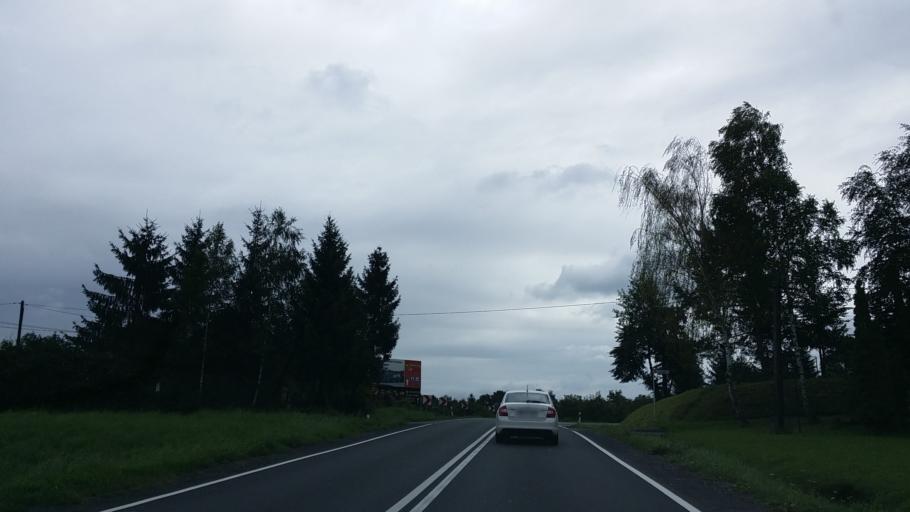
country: PL
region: Lesser Poland Voivodeship
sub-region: Powiat wadowicki
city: Radocza
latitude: 49.9357
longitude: 19.4628
